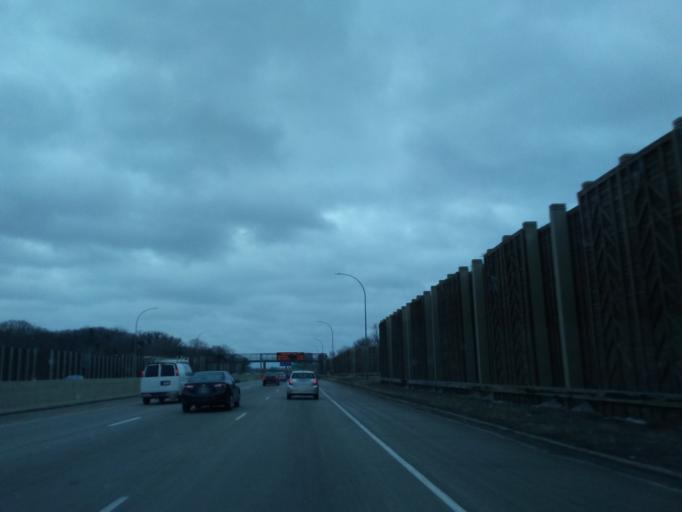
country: US
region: Minnesota
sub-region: Hennepin County
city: Richfield
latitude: 44.8730
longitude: -93.2989
